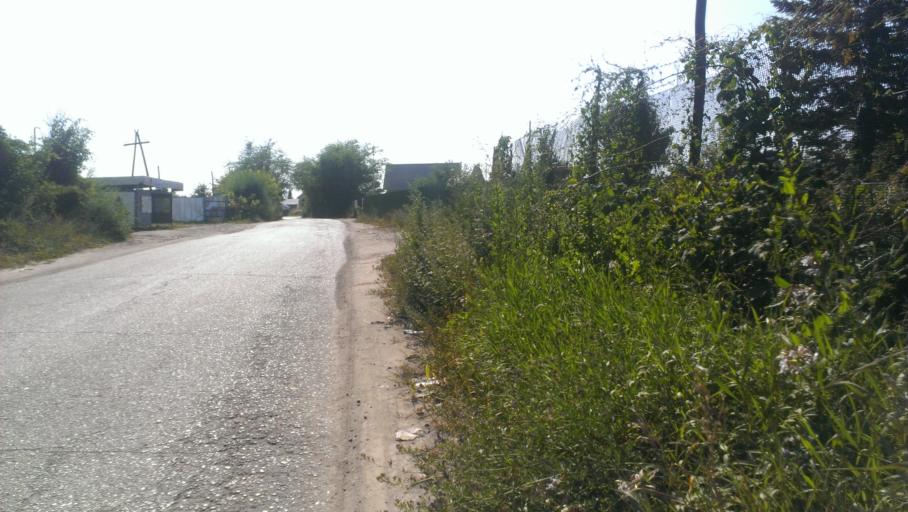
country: RU
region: Altai Krai
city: Novosilikatnyy
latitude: 53.3230
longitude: 83.6831
